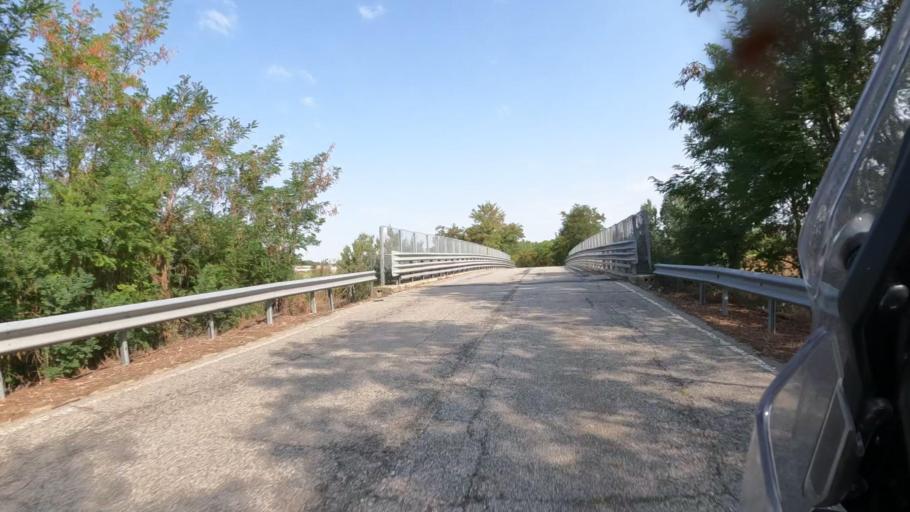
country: IT
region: Piedmont
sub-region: Provincia di Alessandria
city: Quattordio
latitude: 44.9074
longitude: 8.4002
